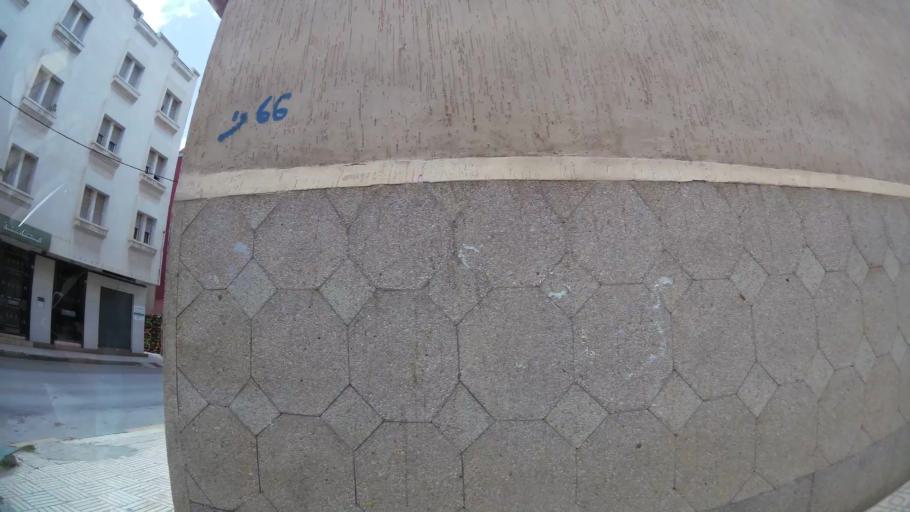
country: MA
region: Oriental
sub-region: Nador
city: Nador
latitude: 35.1689
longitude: -2.9225
